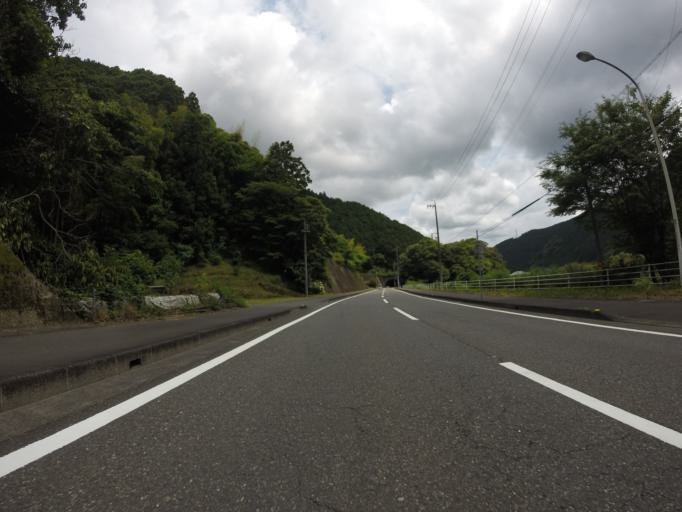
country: JP
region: Shizuoka
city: Shizuoka-shi
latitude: 35.0040
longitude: 138.2860
